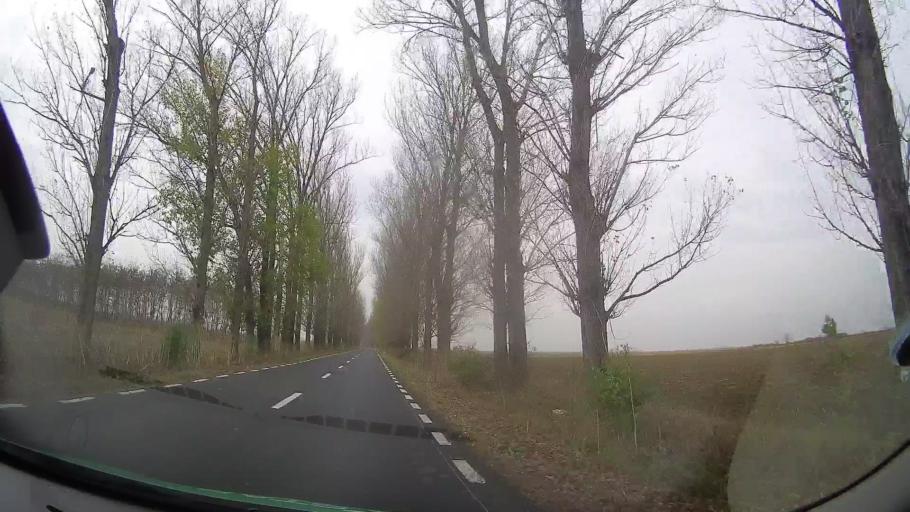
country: RO
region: Ilfov
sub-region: Comuna Nuci
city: Nuci
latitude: 44.7211
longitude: 26.2857
